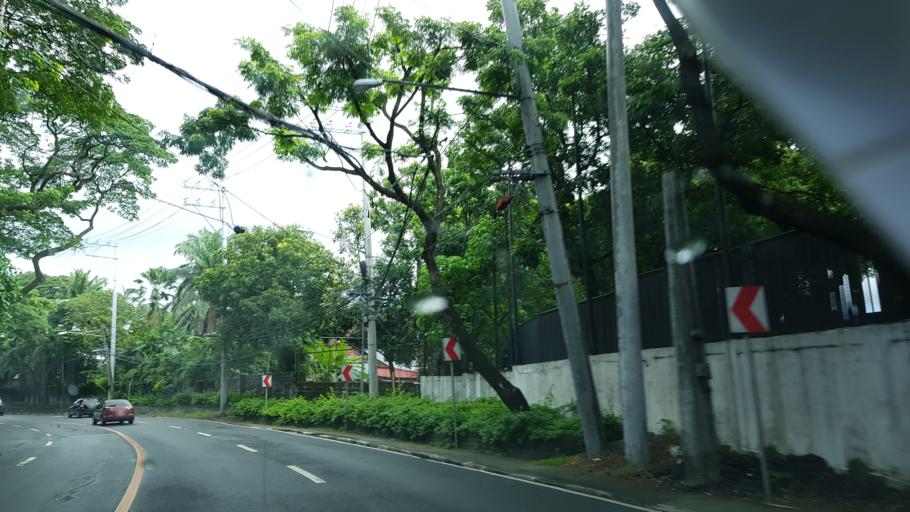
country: PH
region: Metro Manila
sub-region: Makati City
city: Makati City
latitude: 14.5475
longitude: 121.0409
